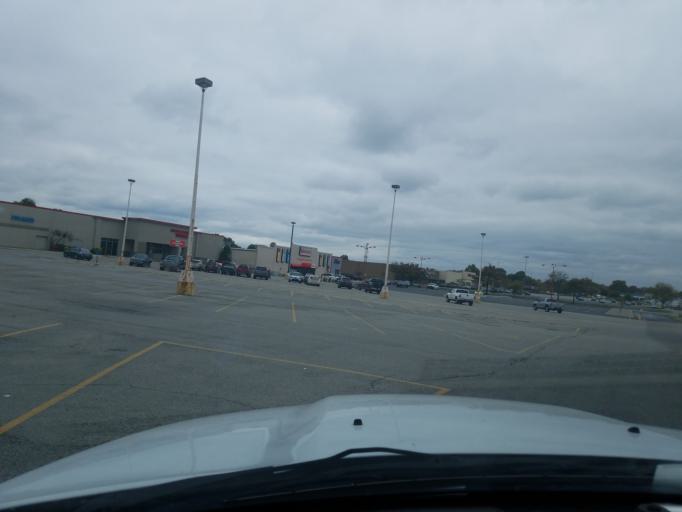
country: US
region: Indiana
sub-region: Clark County
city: Clarksville
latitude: 38.3124
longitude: -85.7628
